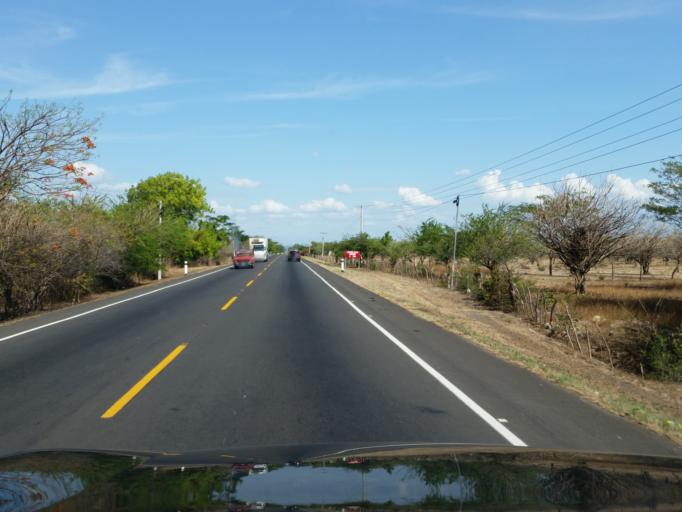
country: NI
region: Leon
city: La Paz Centro
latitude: 12.3203
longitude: -86.7943
